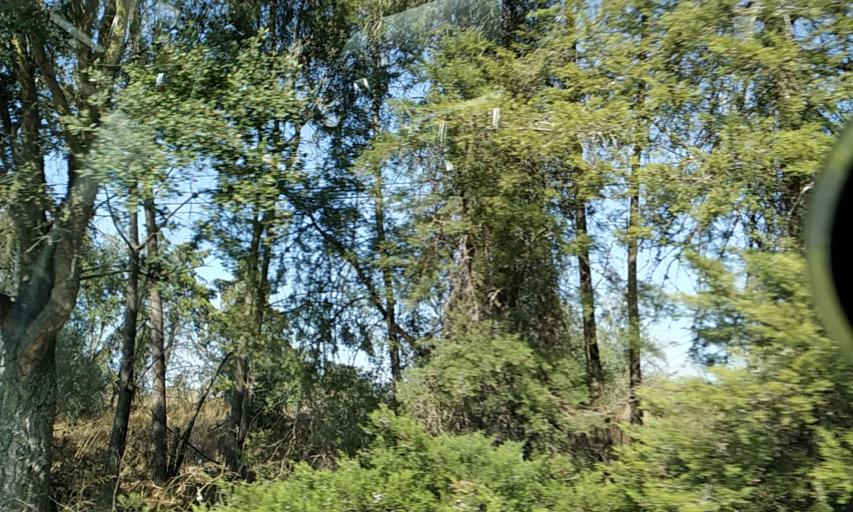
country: PT
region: Santarem
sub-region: Benavente
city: Poceirao
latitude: 38.7522
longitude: -8.6316
